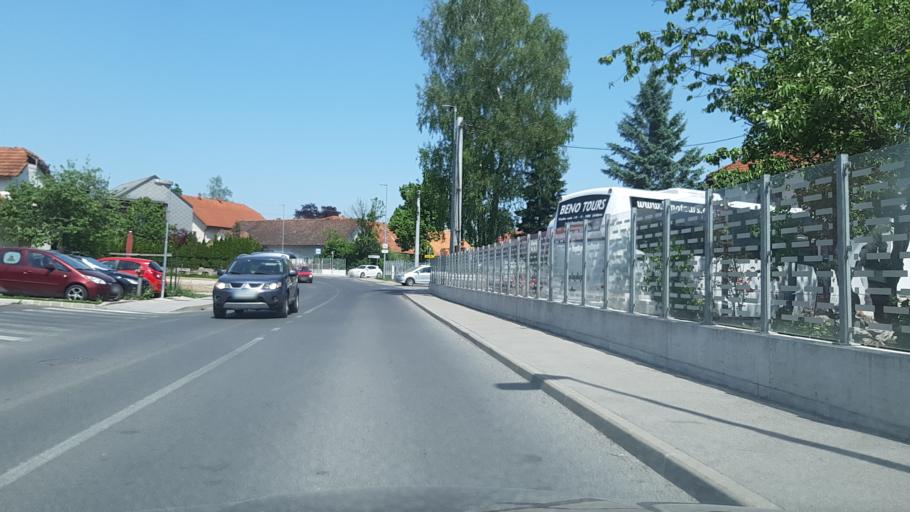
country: SI
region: Brezovica
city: Notranje Gorice
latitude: 45.9738
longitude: 14.4206
